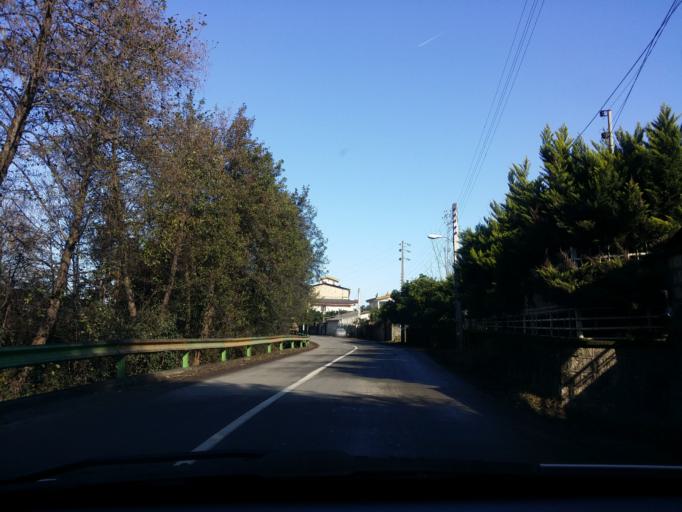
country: IR
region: Mazandaran
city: Chalus
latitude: 36.6840
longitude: 51.3133
